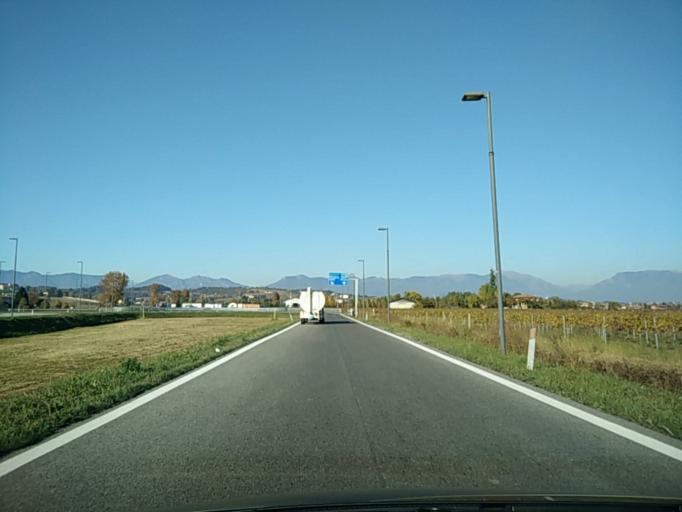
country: IT
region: Veneto
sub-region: Provincia di Treviso
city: Susegana
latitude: 45.8385
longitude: 12.2547
